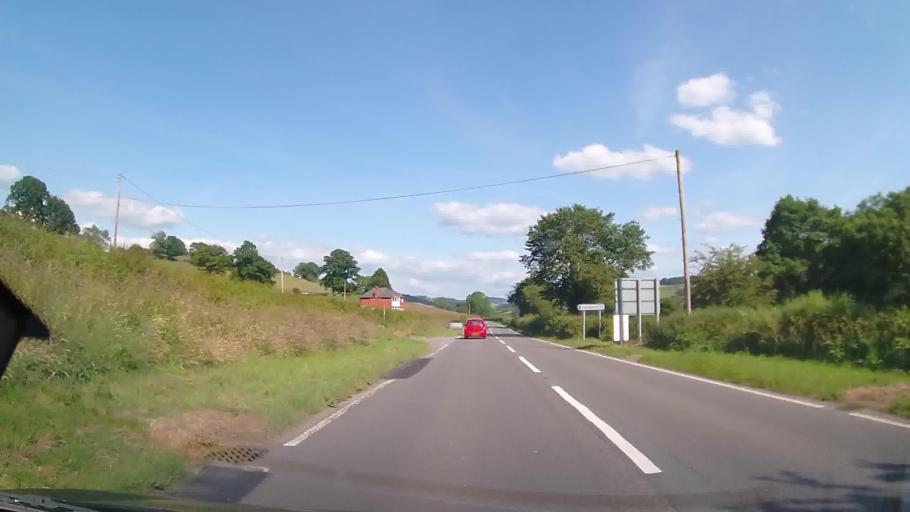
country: GB
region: Wales
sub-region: Sir Powys
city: Llanfyllin
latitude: 52.6658
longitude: -3.3004
